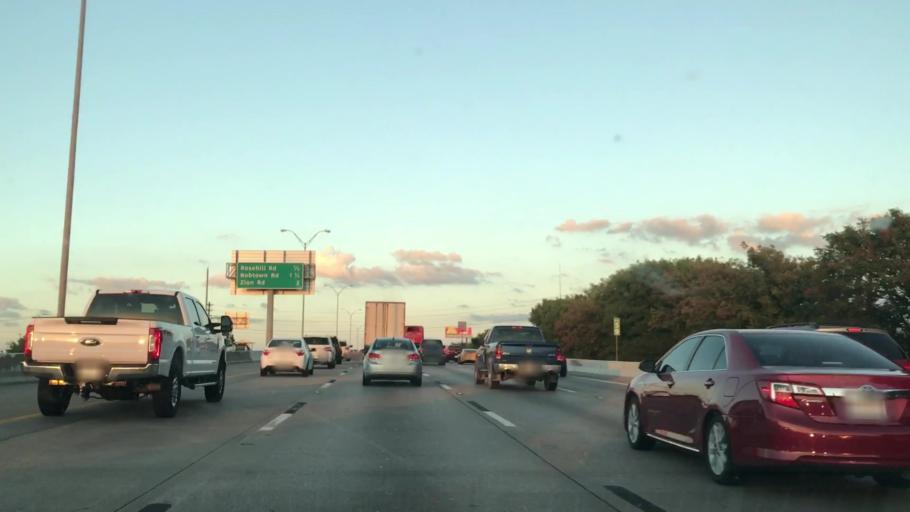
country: US
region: Texas
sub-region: Dallas County
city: Sunnyvale
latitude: 32.8390
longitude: -96.5979
